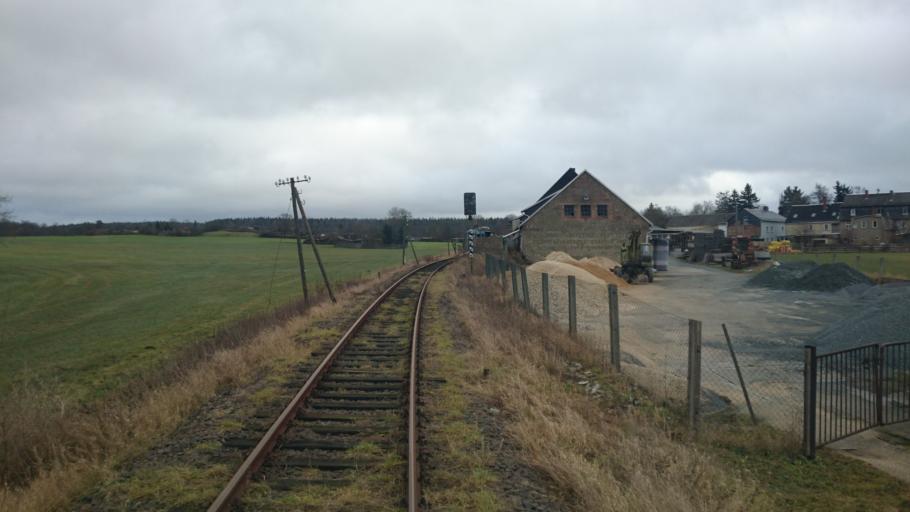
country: DE
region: Saxony
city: Muhltroff
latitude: 50.5431
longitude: 11.9306
